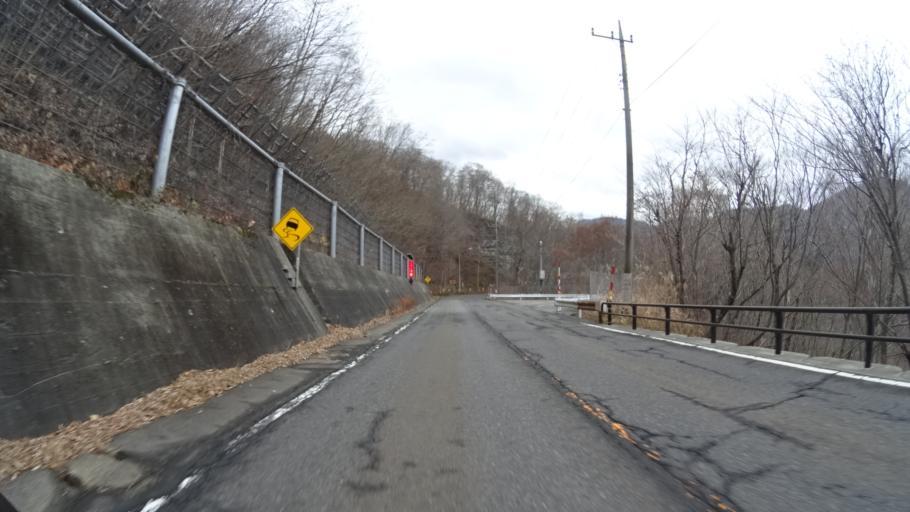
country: JP
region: Gunma
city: Nakanojomachi
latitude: 36.7444
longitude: 138.8356
